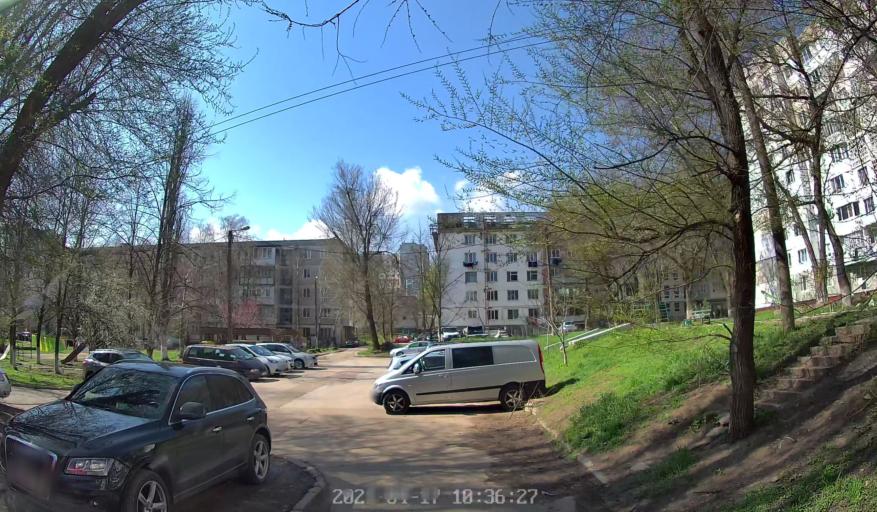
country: MD
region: Chisinau
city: Chisinau
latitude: 47.0358
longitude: 28.8810
